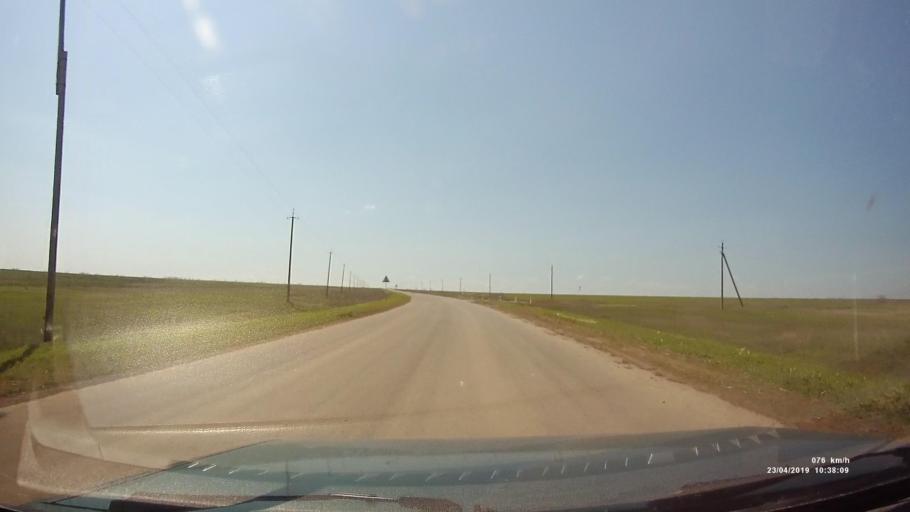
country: RU
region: Kalmykiya
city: Yashalta
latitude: 46.5363
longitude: 42.6390
